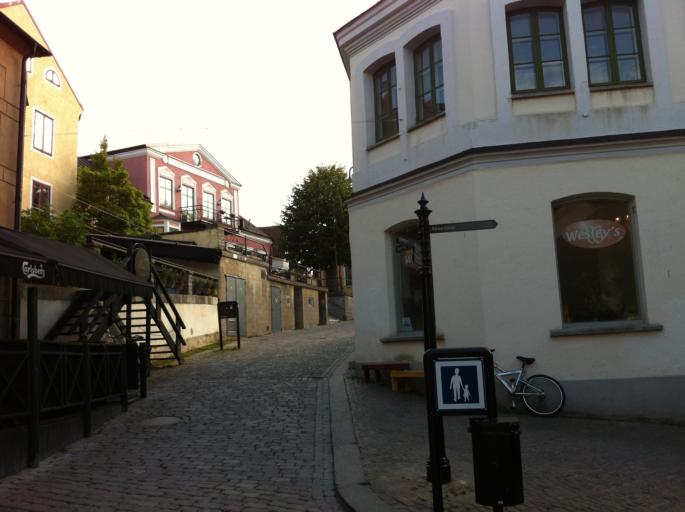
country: SE
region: Gotland
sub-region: Gotland
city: Visby
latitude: 57.6387
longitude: 18.2959
